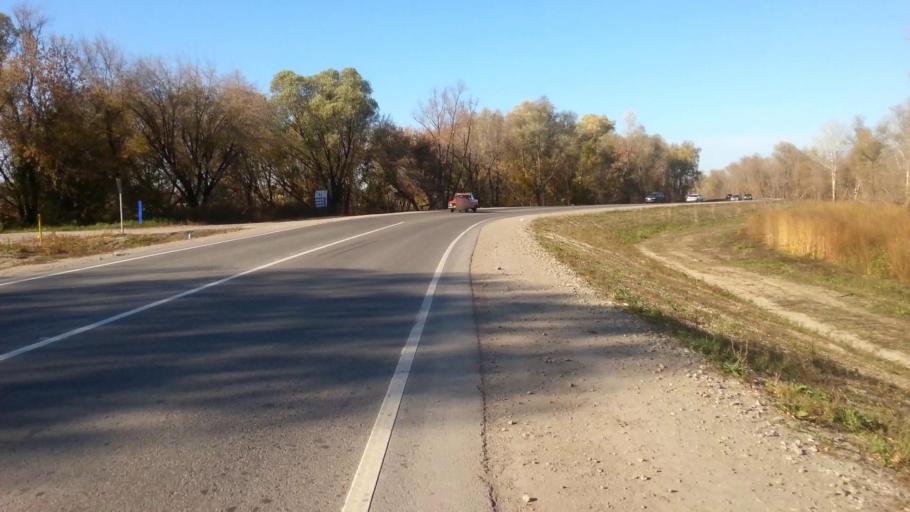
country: RU
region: Altai Krai
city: Sannikovo
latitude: 53.3216
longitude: 83.9429
